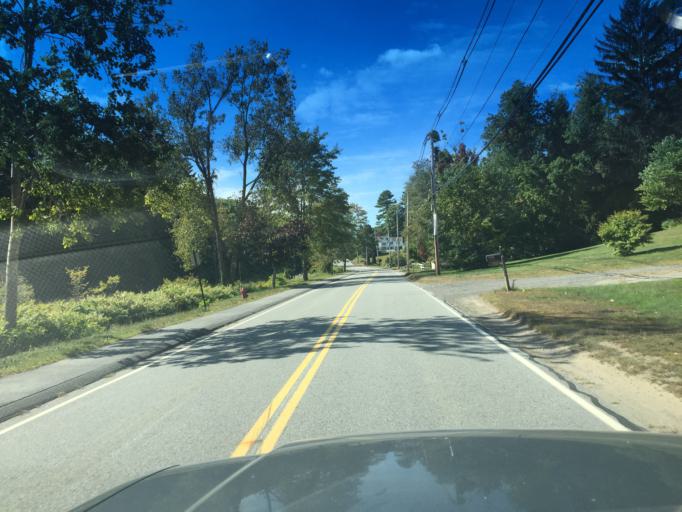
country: US
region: Massachusetts
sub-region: Worcester County
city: Northborough
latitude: 42.3281
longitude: -71.6323
